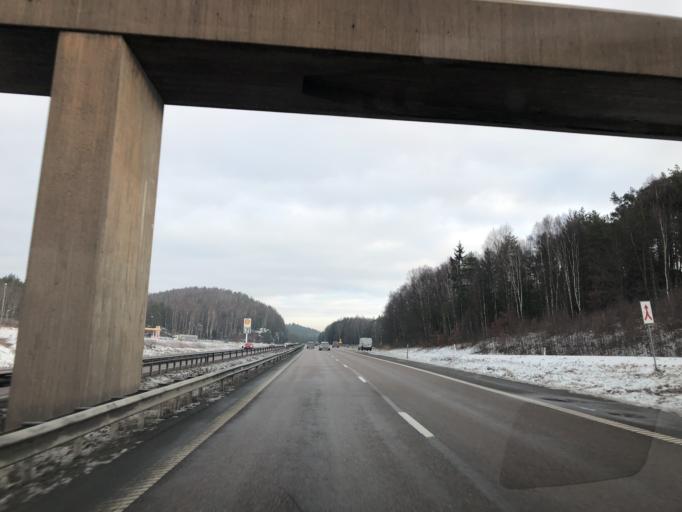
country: SE
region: Vaestra Goetaland
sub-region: Molndal
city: Lindome
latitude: 57.5524
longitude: 12.0532
